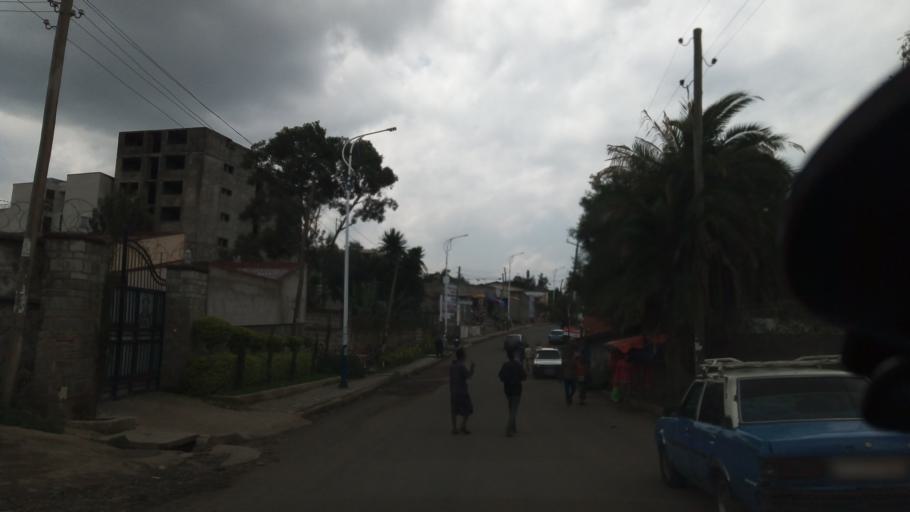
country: ET
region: Adis Abeba
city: Addis Ababa
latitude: 8.9943
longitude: 38.7159
